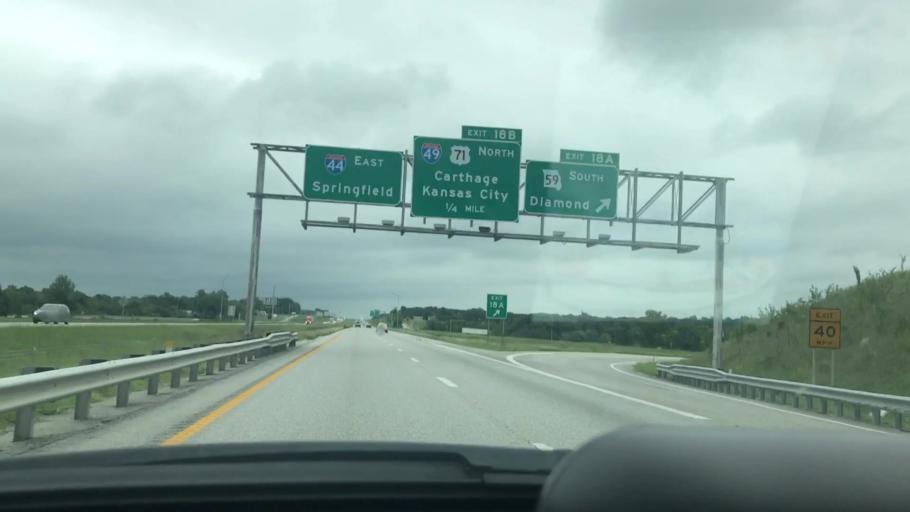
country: US
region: Missouri
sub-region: Jasper County
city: Carthage
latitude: 37.0818
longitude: -94.3167
